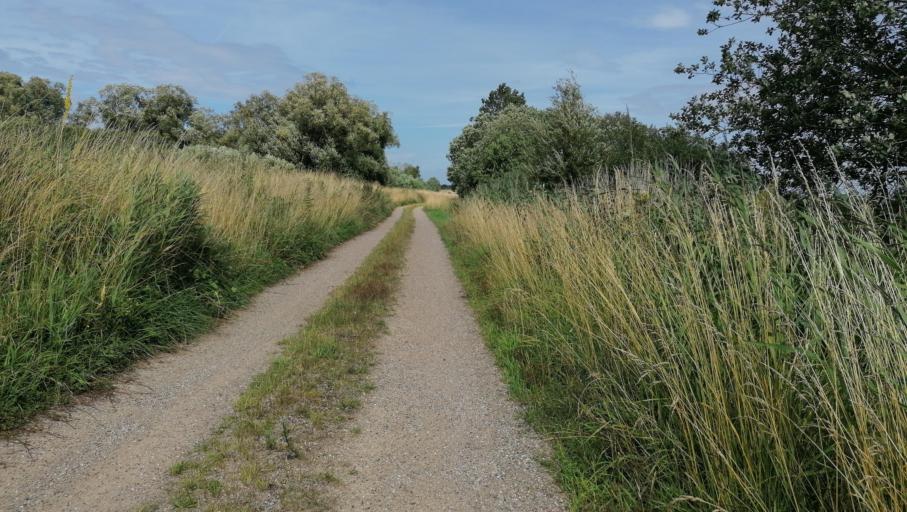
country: DK
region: Zealand
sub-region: Odsherred Kommune
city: Horve
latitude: 55.7841
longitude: 11.4201
